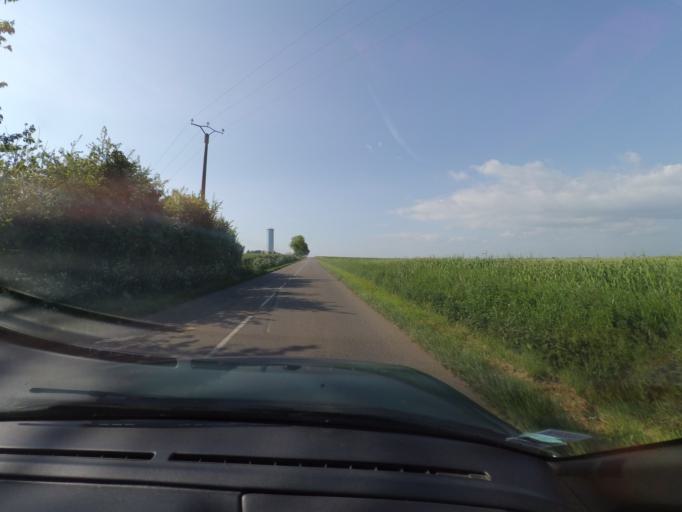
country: FR
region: Pays de la Loire
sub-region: Departement de la Vendee
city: Angles
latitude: 46.4100
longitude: -1.3849
